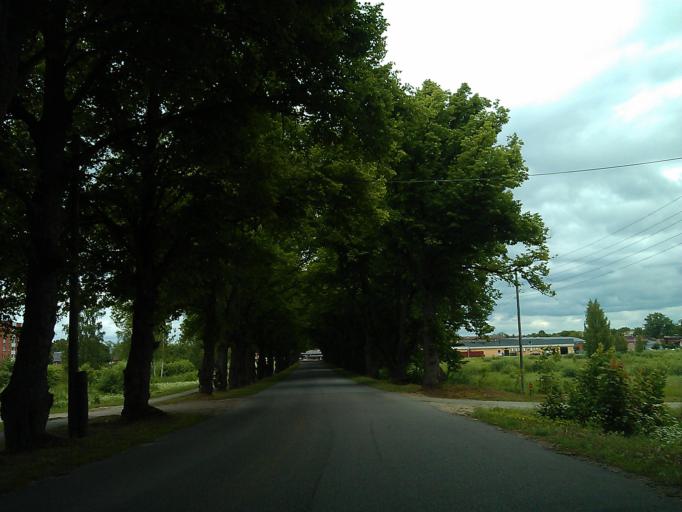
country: LV
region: Kuldigas Rajons
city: Kuldiga
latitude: 56.9644
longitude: 21.9537
